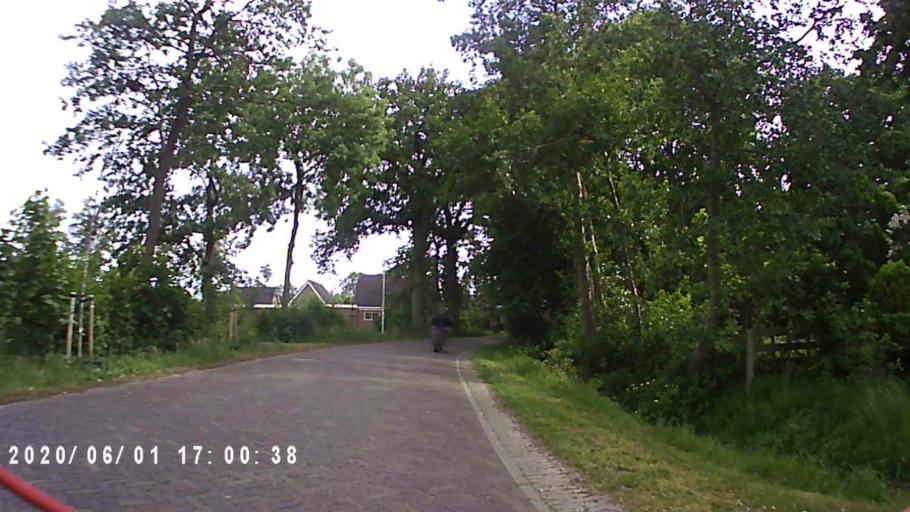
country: NL
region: Friesland
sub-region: Gemeente Tytsjerksteradiel
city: Hurdegaryp
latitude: 53.1825
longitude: 5.9296
